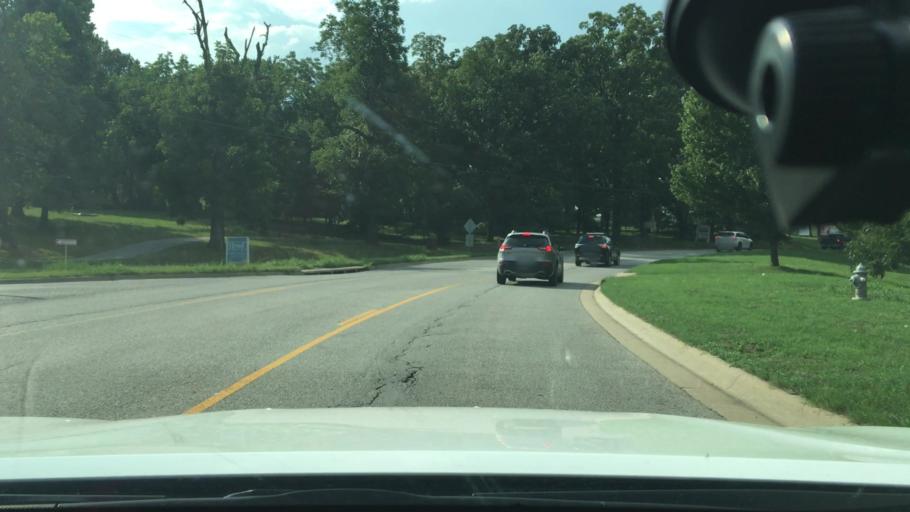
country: US
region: Arkansas
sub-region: Benton County
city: Bentonville
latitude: 36.3311
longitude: -94.1883
